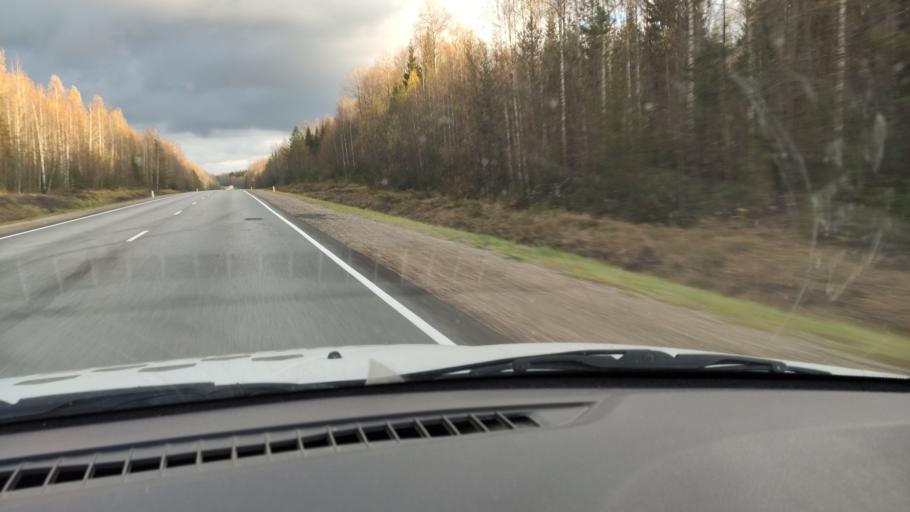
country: RU
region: Kirov
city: Chernaya Kholunitsa
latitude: 58.7836
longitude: 51.9065
